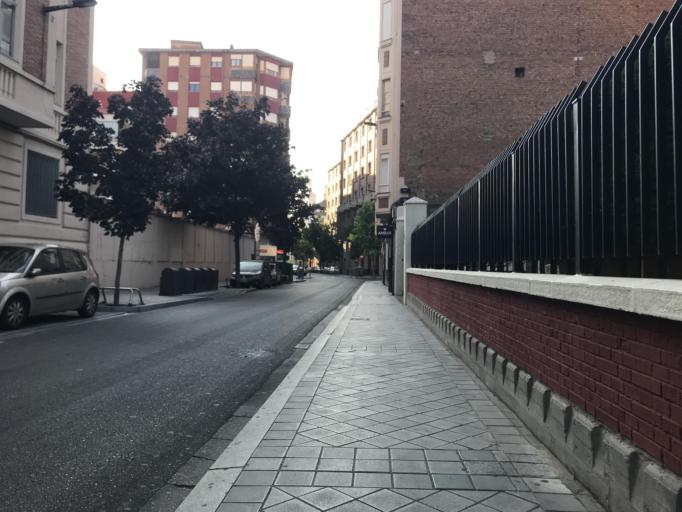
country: ES
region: Castille and Leon
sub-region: Provincia de Valladolid
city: Valladolid
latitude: 41.6499
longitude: -4.7234
